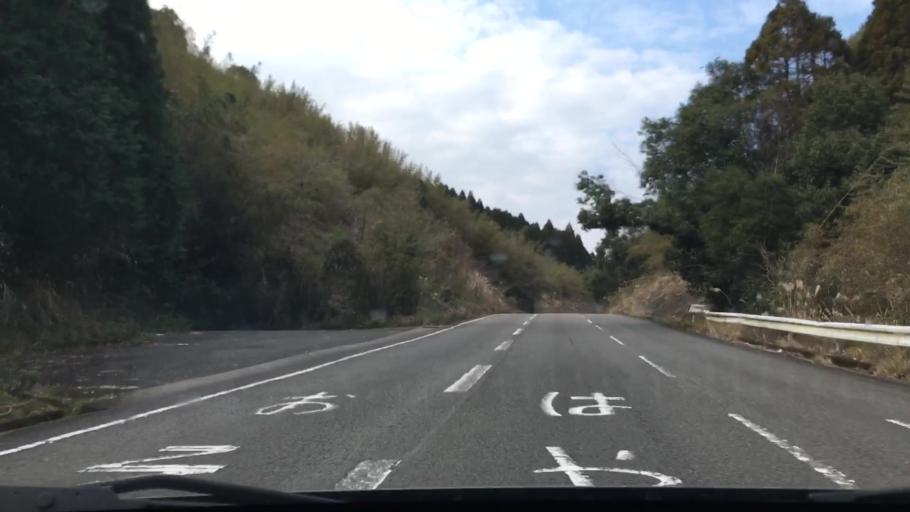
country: JP
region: Miyazaki
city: Nichinan
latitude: 31.6348
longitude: 131.3379
